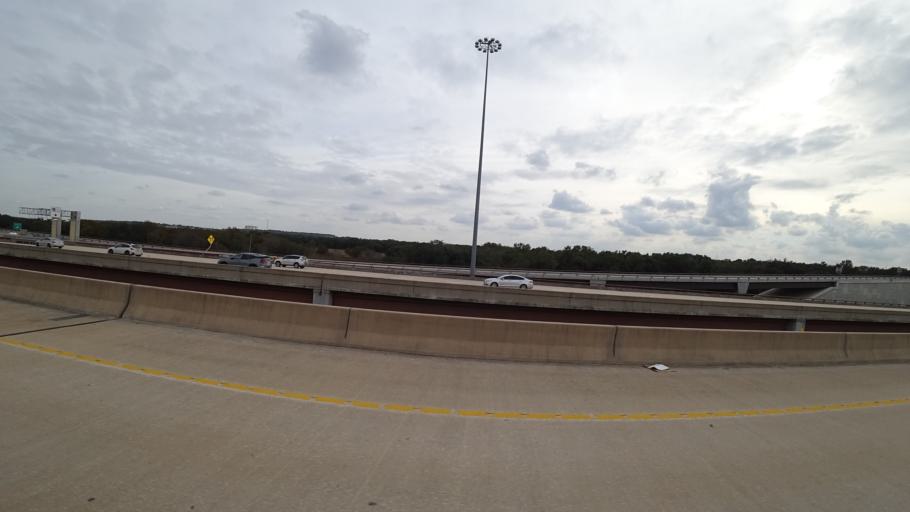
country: US
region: Texas
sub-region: Williamson County
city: Brushy Creek
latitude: 30.4800
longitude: -97.7165
